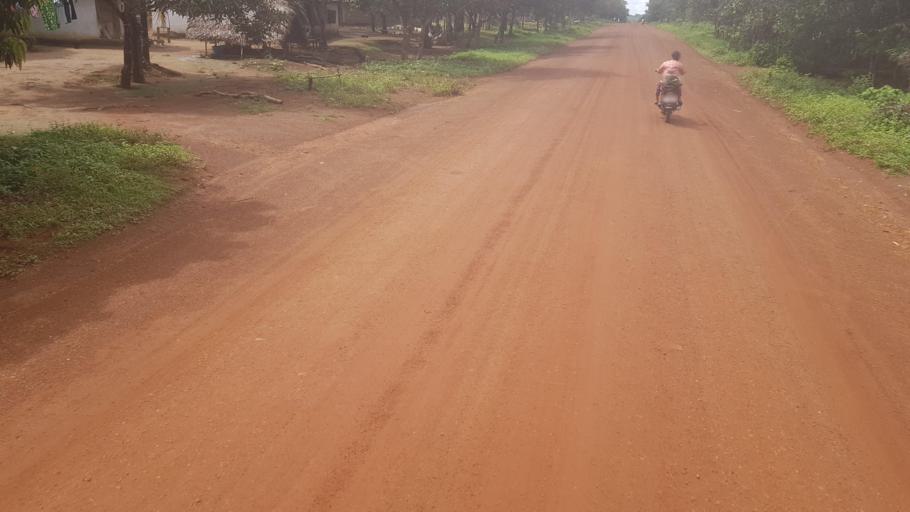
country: SL
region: Southern Province
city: Mogbwemo
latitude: 7.7515
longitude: -12.3080
